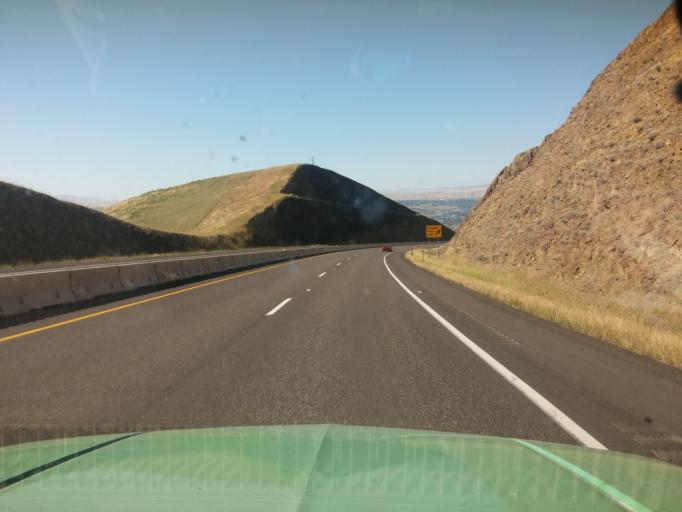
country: US
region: Idaho
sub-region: Nez Perce County
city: Lewiston
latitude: 46.4509
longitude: -116.9708
